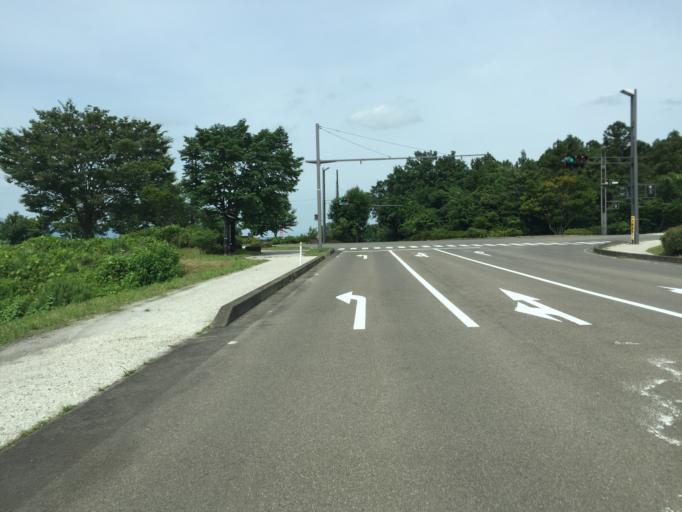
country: JP
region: Fukushima
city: Fukushima-shi
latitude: 37.7360
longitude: 140.3842
